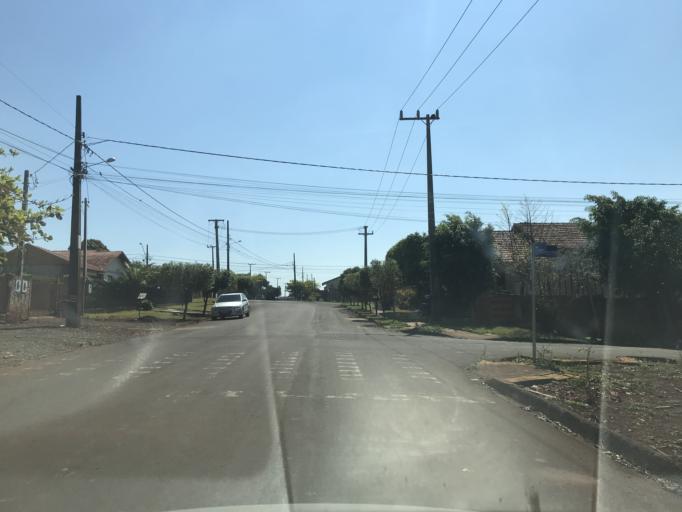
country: BR
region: Parana
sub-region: Palotina
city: Palotina
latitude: -24.3000
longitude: -53.8308
